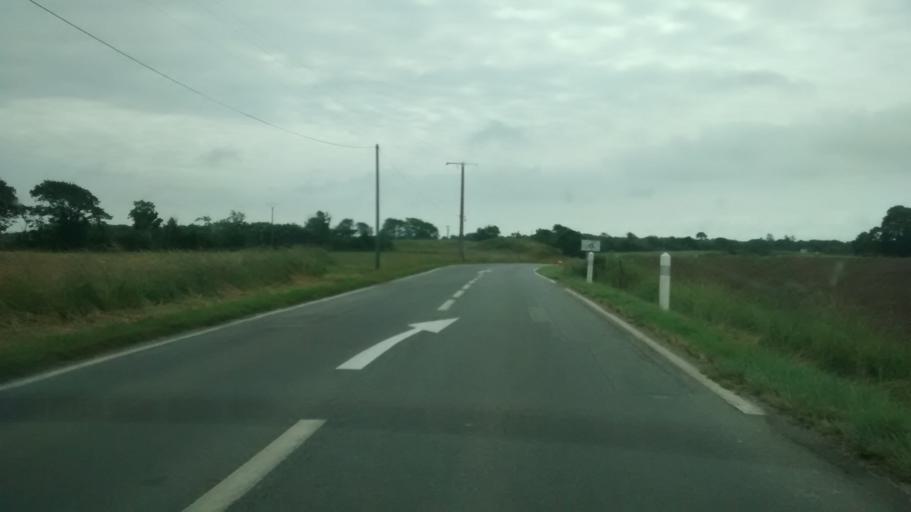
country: FR
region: Brittany
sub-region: Departement du Morbihan
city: Ploemeur
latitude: 47.7531
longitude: -3.4199
